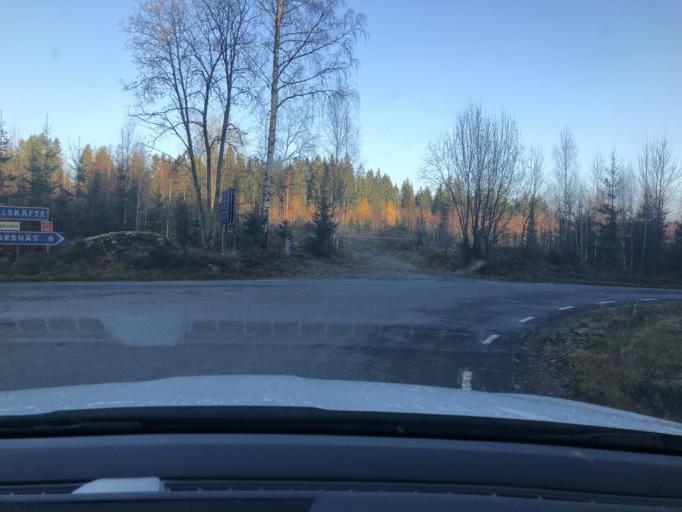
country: SE
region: Soedermanland
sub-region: Flens Kommun
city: Halleforsnas
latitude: 59.1156
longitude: 16.4369
